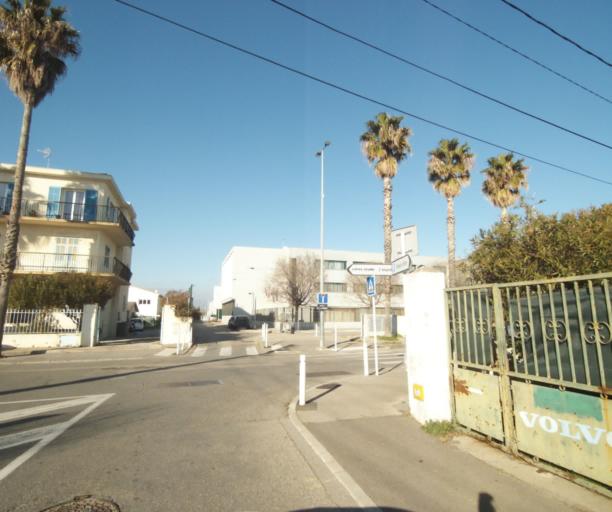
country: FR
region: Provence-Alpes-Cote d'Azur
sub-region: Departement des Alpes-Maritimes
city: Antibes
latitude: 43.5995
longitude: 7.1242
